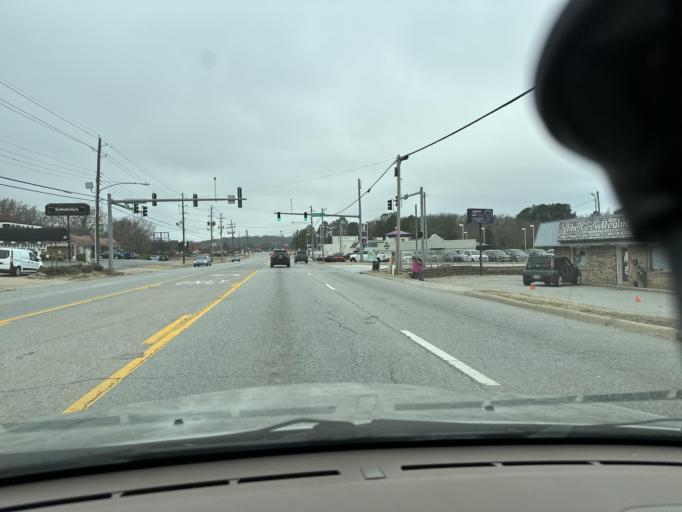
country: US
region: Arkansas
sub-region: Washington County
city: Fayetteville
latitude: 36.0986
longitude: -94.1510
